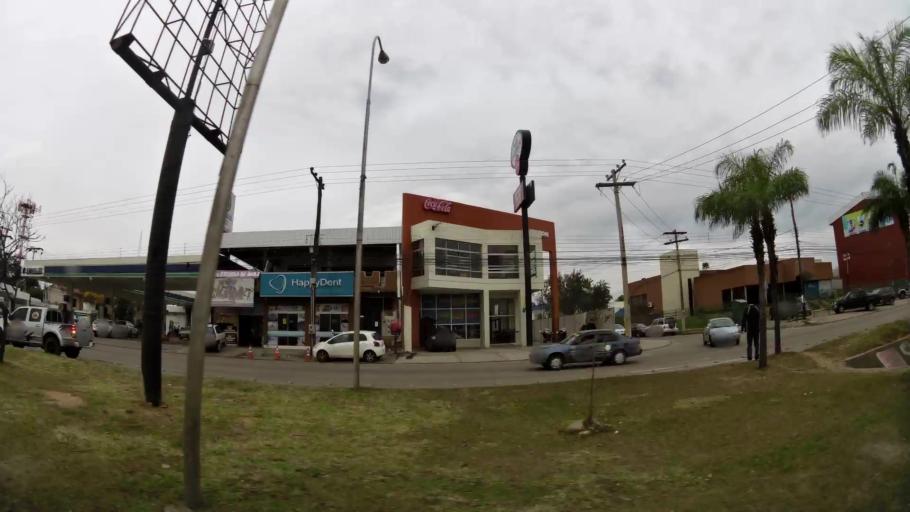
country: BO
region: Santa Cruz
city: Santa Cruz de la Sierra
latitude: -17.8166
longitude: -63.1835
